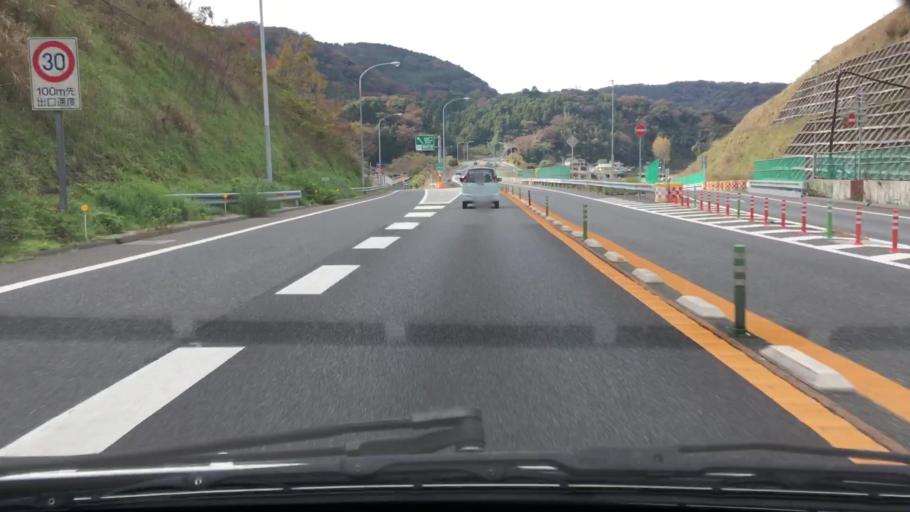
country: JP
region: Chiba
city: Futtsu
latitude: 35.1974
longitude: 139.8620
